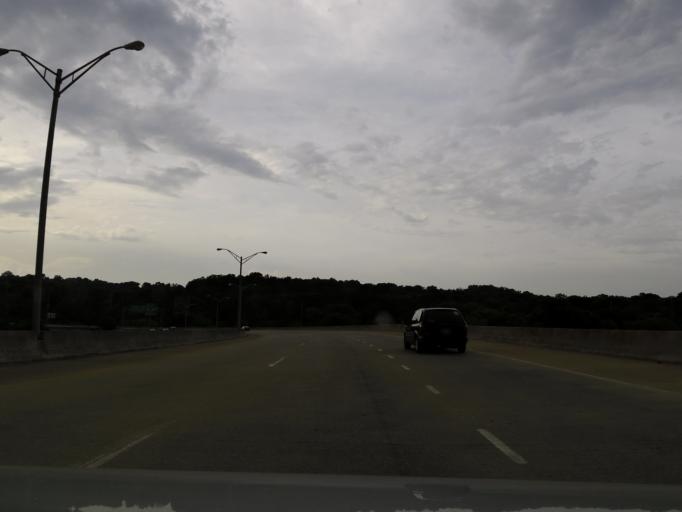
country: US
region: Tennessee
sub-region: Knox County
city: Knoxville
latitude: 35.9626
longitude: -83.8972
